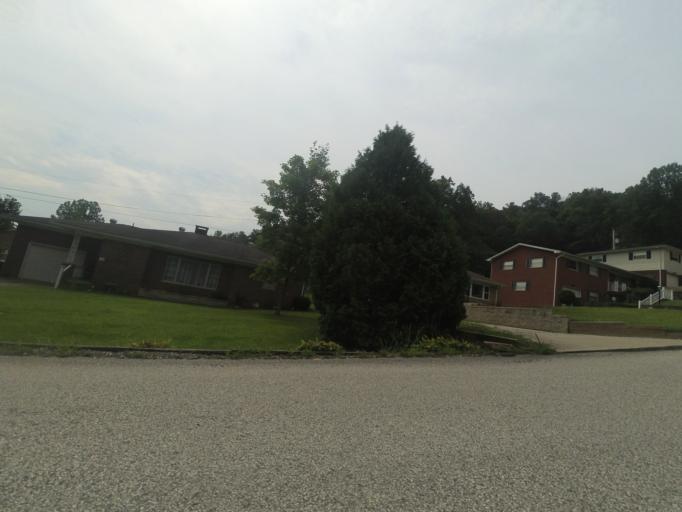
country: US
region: West Virginia
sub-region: Cabell County
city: Huntington
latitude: 38.4334
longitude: -82.4654
